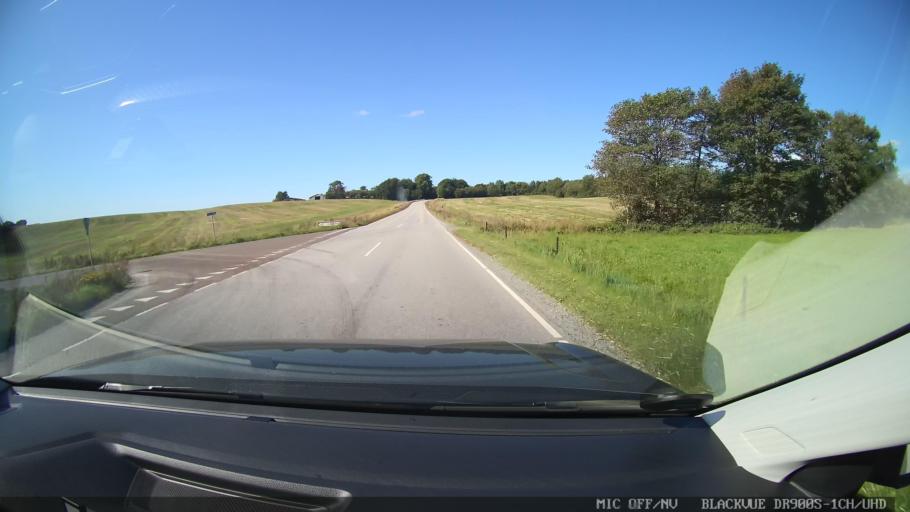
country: DK
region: North Denmark
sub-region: Mariagerfjord Kommune
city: Mariager
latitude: 56.6207
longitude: 9.9809
